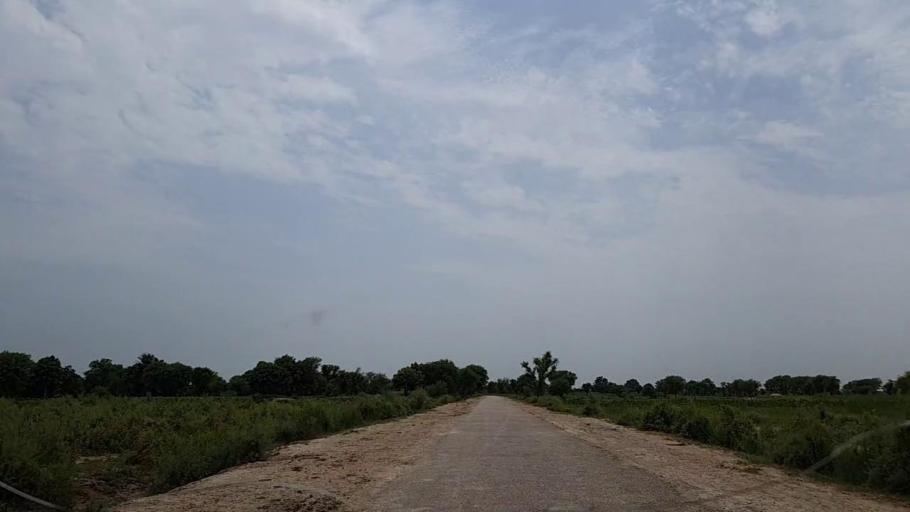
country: PK
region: Sindh
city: Tharu Shah
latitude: 26.9145
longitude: 68.0953
